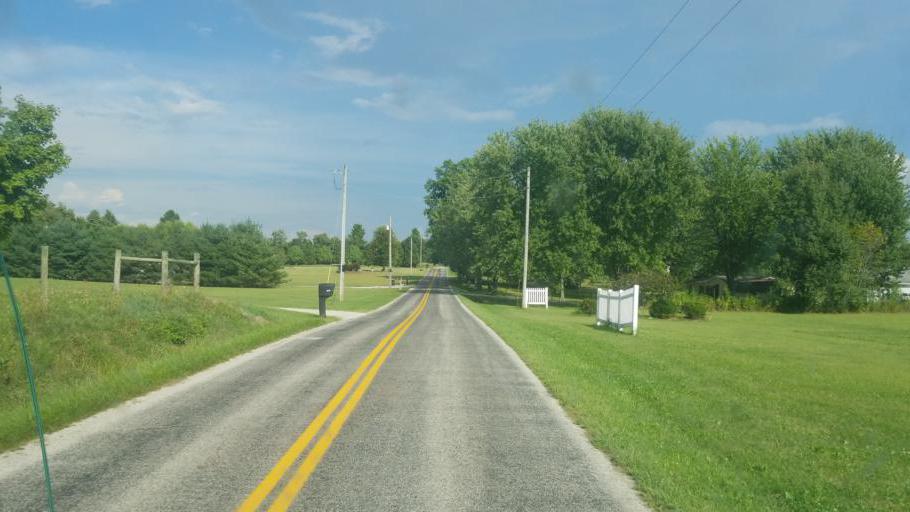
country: US
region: Ohio
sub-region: Huron County
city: Plymouth
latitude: 41.0053
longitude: -82.6425
